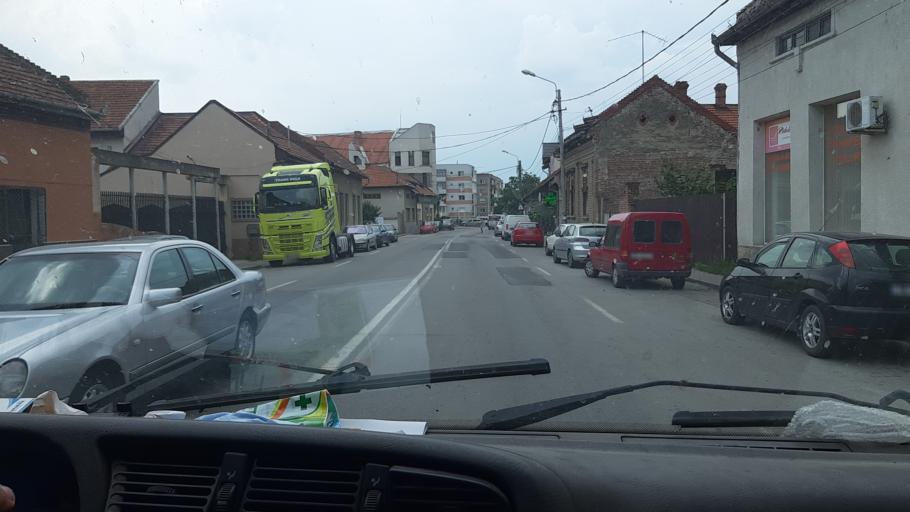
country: RO
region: Timis
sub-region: Municipiul Lugoj
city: Lugoj
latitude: 45.6914
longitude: 21.9028
